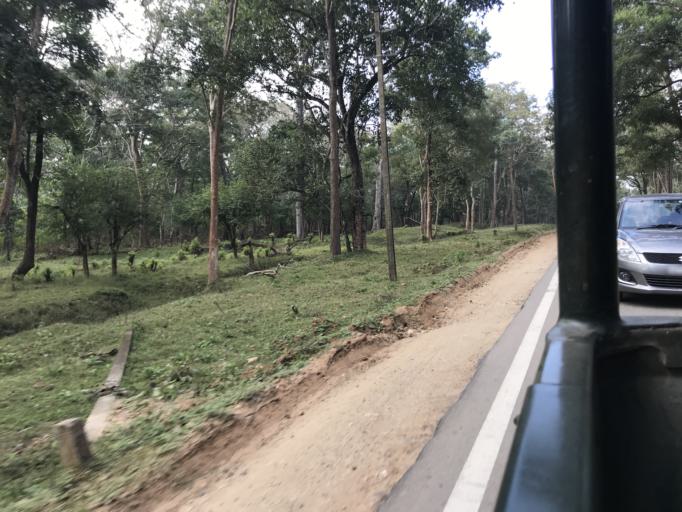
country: IN
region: Karnataka
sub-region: Mysore
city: Heggadadevankote
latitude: 11.9371
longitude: 76.2014
